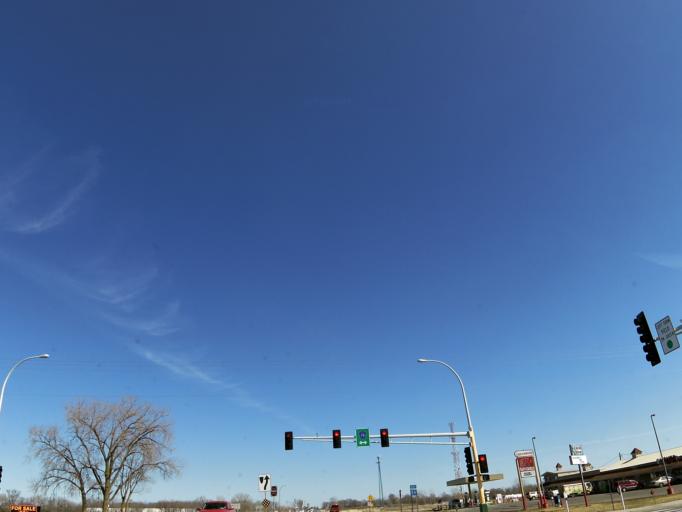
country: US
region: Minnesota
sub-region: Hennepin County
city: Medina
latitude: 45.0654
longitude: -93.6357
